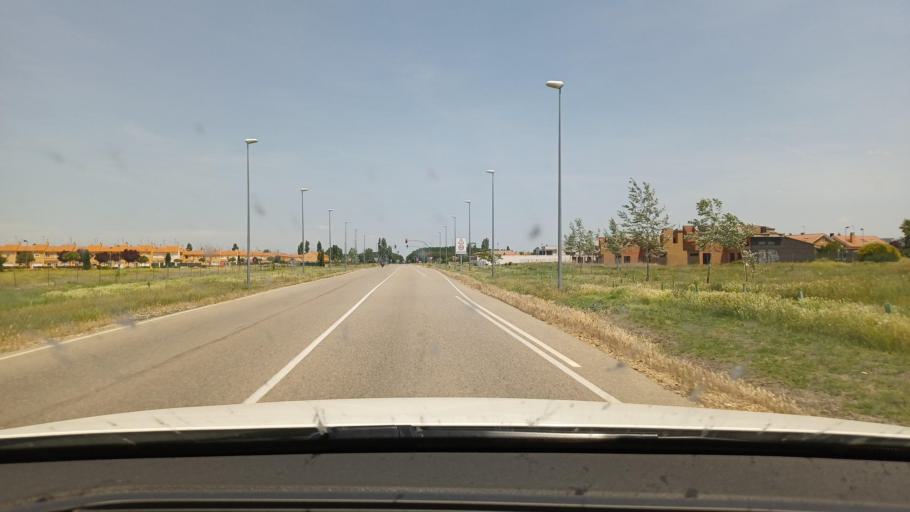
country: ES
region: Castille and Leon
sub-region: Provincia de Valladolid
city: Aldeamayor de San Martin
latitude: 41.5246
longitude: -4.6295
